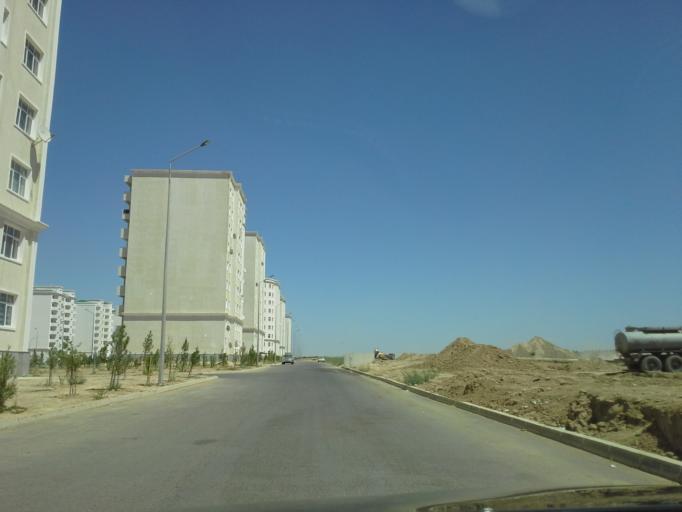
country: TM
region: Ahal
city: Ashgabat
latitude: 37.8856
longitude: 58.4068
